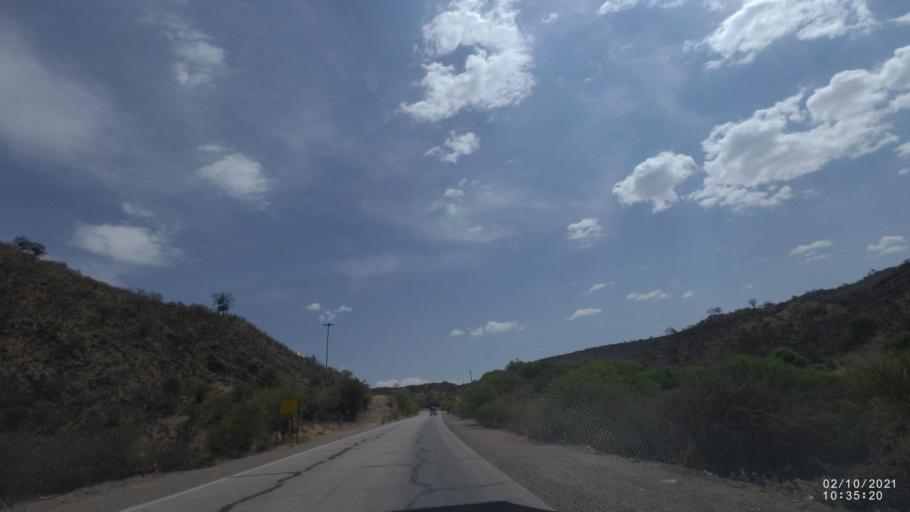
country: BO
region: Cochabamba
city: Capinota
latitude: -17.6625
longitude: -66.2577
